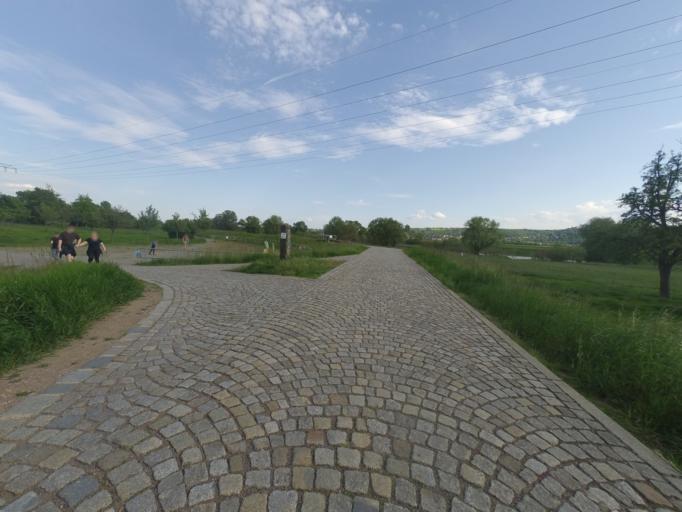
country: DE
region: Saxony
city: Radebeul
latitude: 51.1036
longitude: 13.6293
